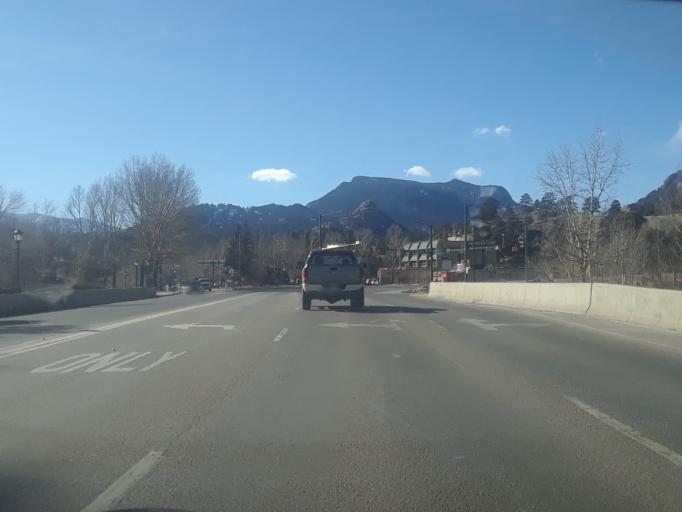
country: US
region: Colorado
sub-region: Larimer County
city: Estes Park
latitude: 40.3779
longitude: -105.5151
